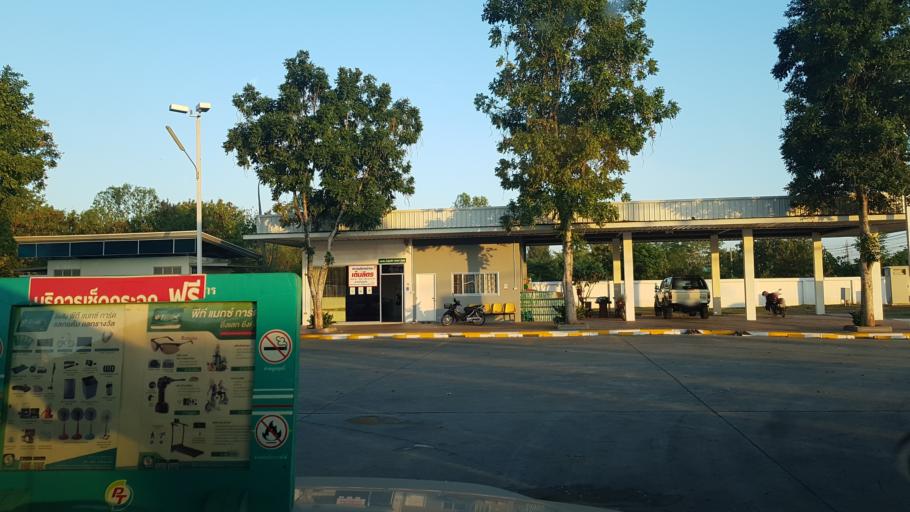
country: TH
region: Khon Kaen
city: Chum Phae
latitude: 16.5809
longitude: 102.0196
